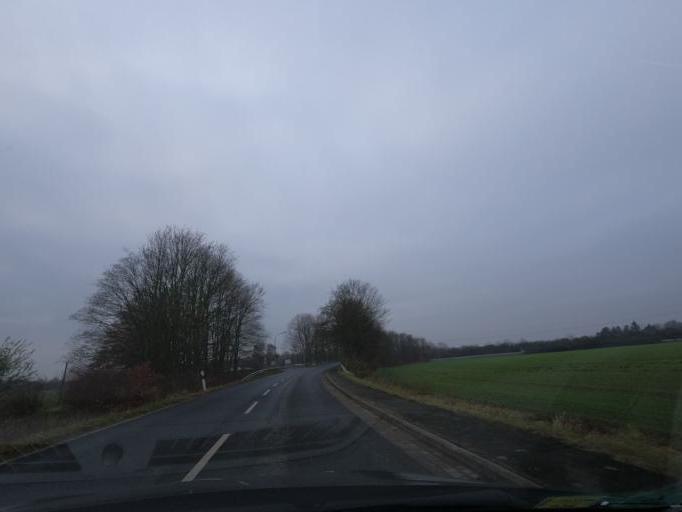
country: DE
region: Lower Saxony
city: Leiferde
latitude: 52.2027
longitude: 10.5347
